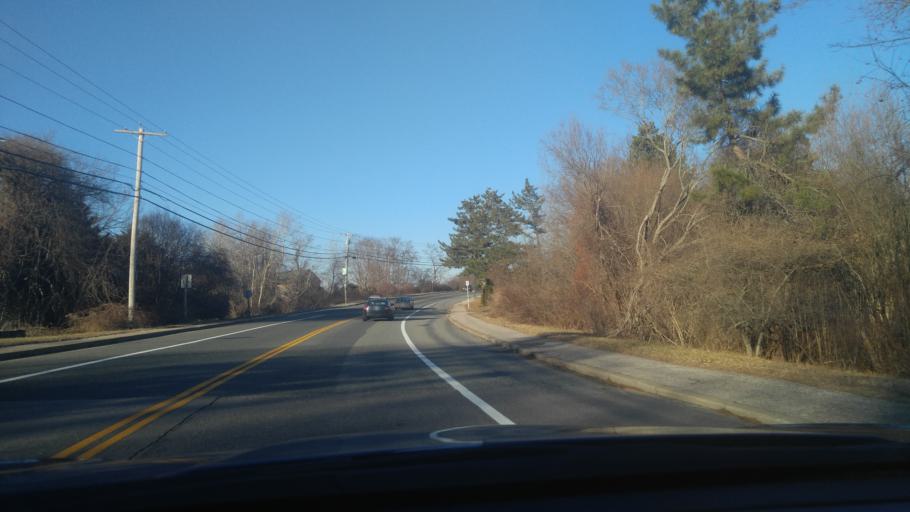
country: US
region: Rhode Island
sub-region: Washington County
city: Narragansett Pier
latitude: 41.4473
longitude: -71.4511
